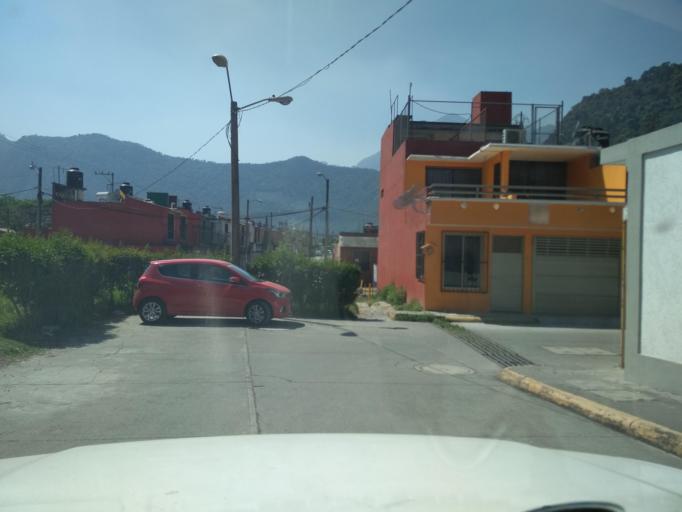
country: MX
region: Veracruz
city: Jalapilla
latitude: 18.8219
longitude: -97.0898
